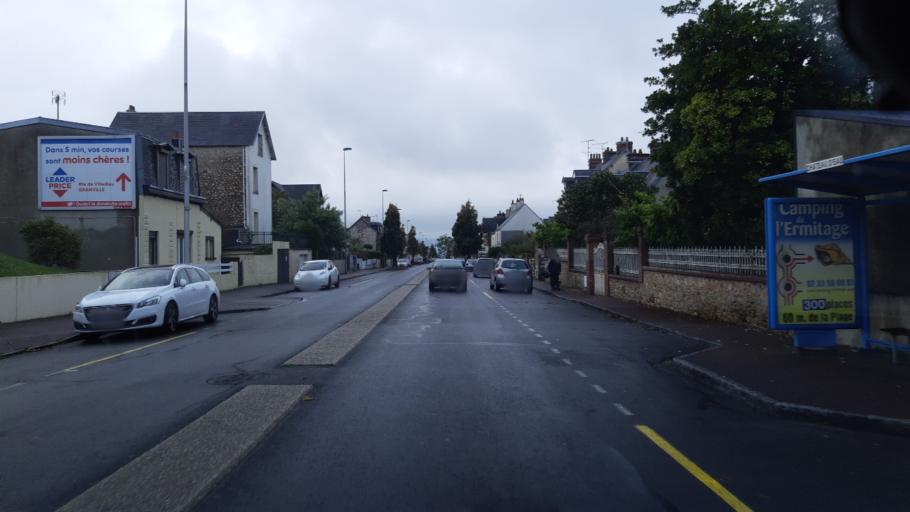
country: FR
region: Lower Normandy
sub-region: Departement de la Manche
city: Donville-les-Bains
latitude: 48.8537
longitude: -1.5658
